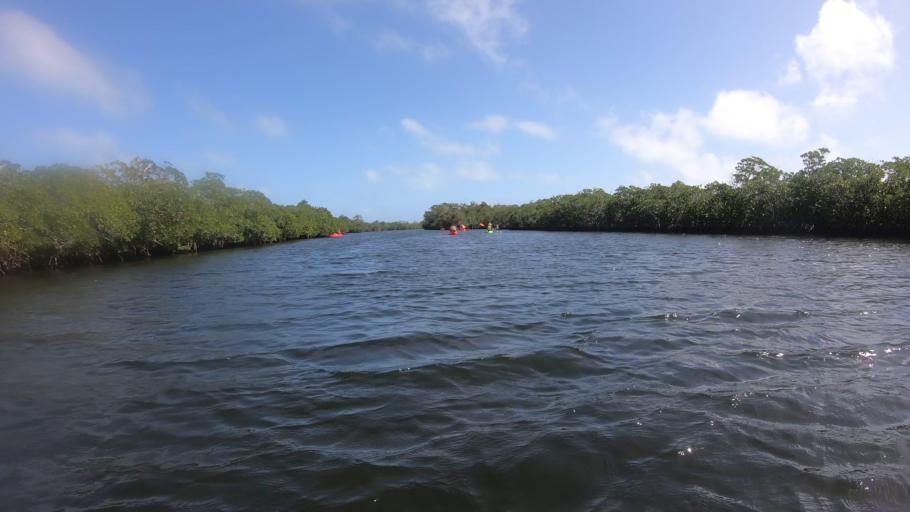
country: US
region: Florida
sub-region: Monroe County
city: Key Largo
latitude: 25.1223
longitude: -80.4053
